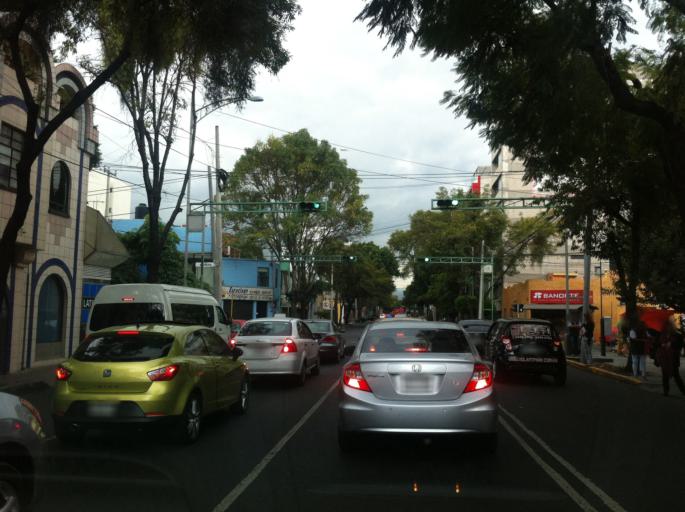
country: MX
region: Mexico City
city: Benito Juarez
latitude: 19.3993
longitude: -99.1626
